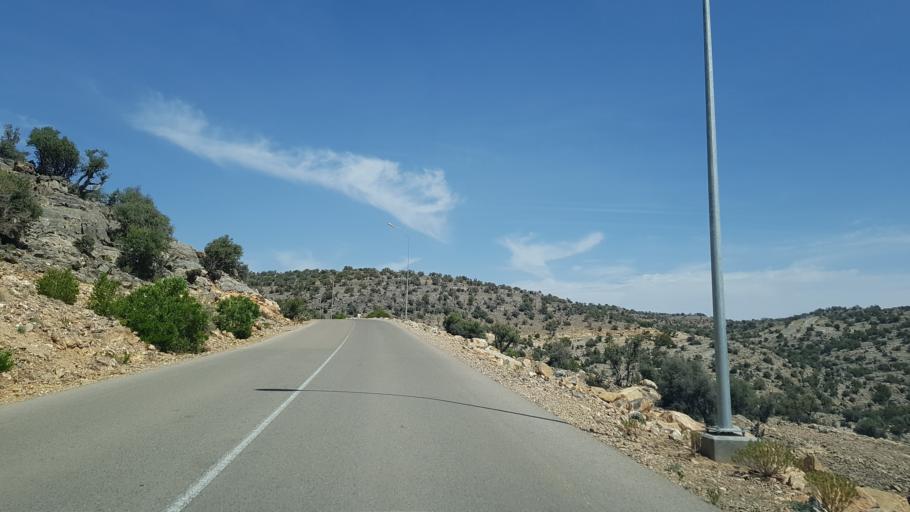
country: OM
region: Al Batinah
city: Bayt al `Awabi
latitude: 23.1403
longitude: 57.5910
